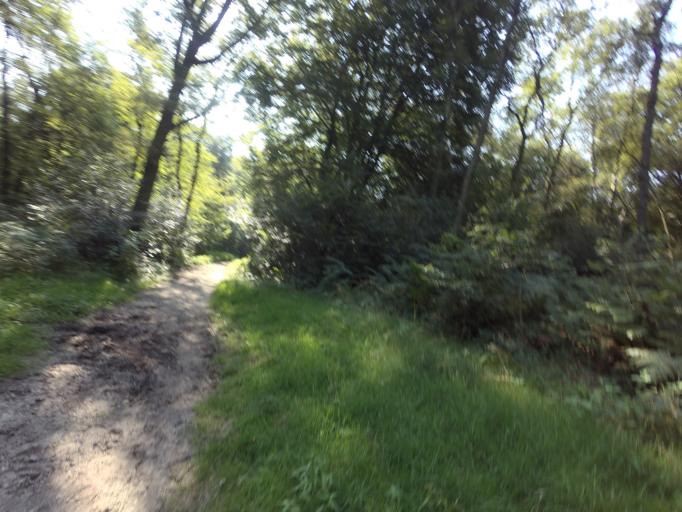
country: BE
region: Wallonia
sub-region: Province de Liege
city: Plombieres
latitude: 50.7656
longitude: 5.9666
